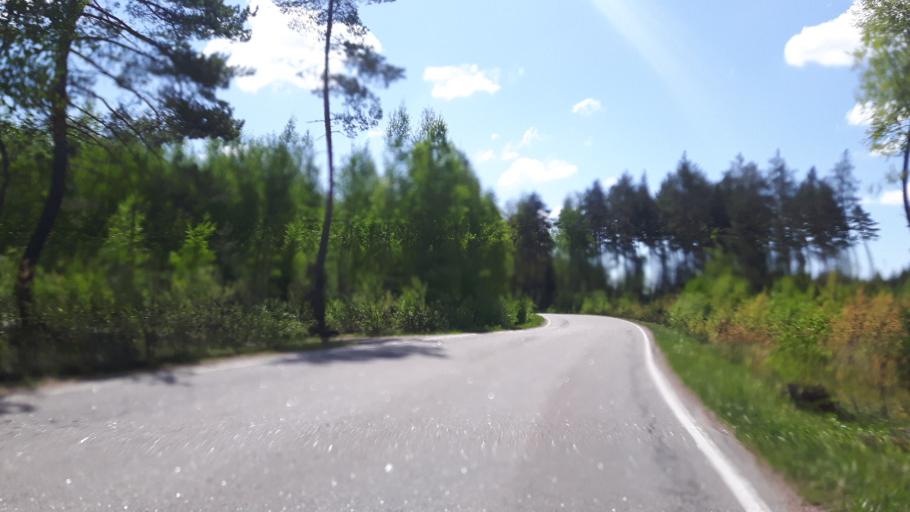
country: FI
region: Kymenlaakso
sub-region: Kotka-Hamina
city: Hamina
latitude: 60.5284
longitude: 27.2952
